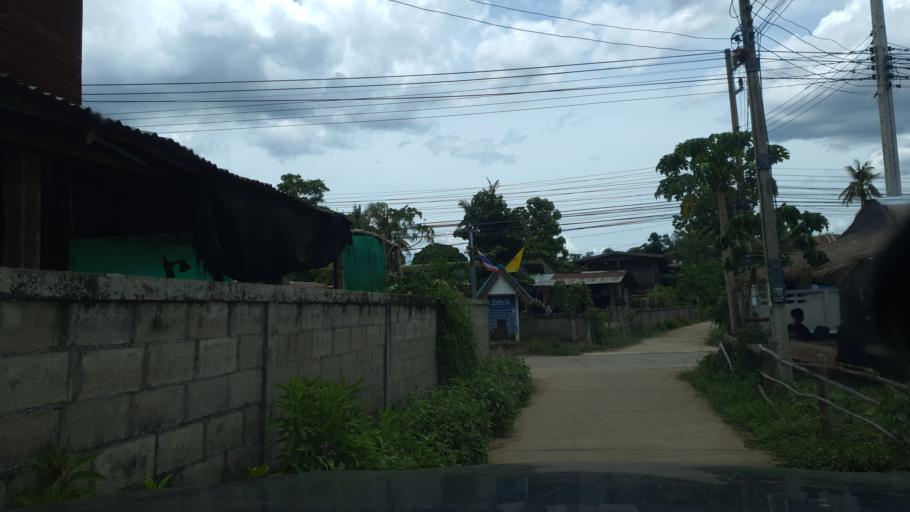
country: TH
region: Sukhothai
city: Thung Saliam
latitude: 17.3133
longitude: 99.5640
